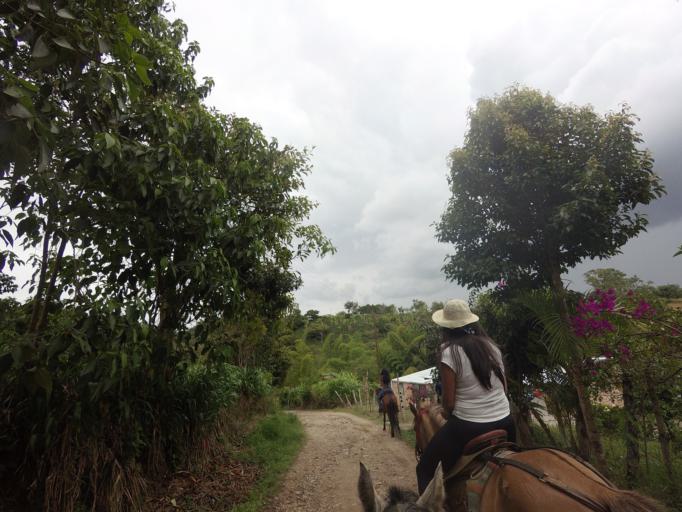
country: CO
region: Huila
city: San Agustin
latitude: 1.8930
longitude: -76.2951
